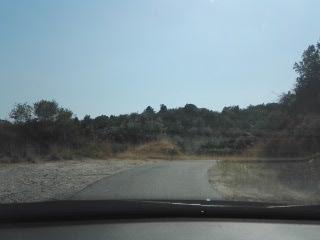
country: IT
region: Calabria
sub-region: Provincia di Reggio Calabria
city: Camini
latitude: 38.4422
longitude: 16.4691
